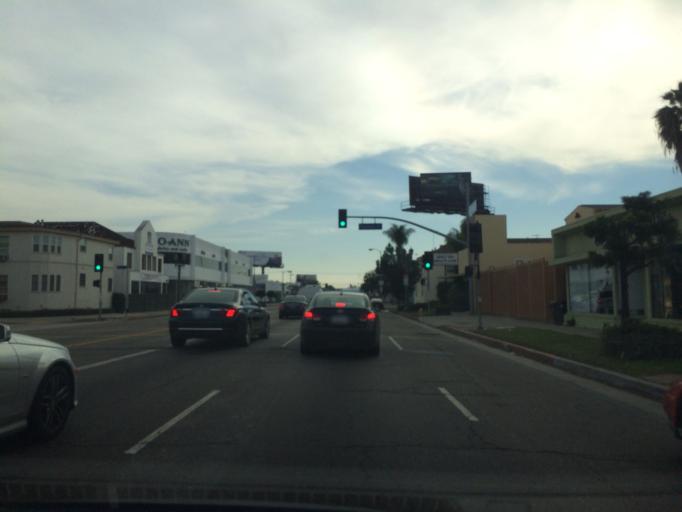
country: US
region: California
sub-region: Los Angeles County
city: Beverly Hills
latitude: 34.0554
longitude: -118.3763
